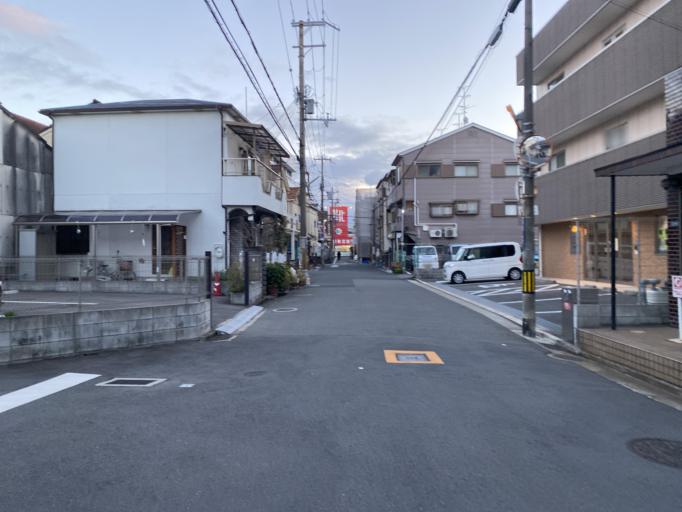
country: JP
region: Osaka
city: Yao
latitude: 34.6712
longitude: 135.5814
